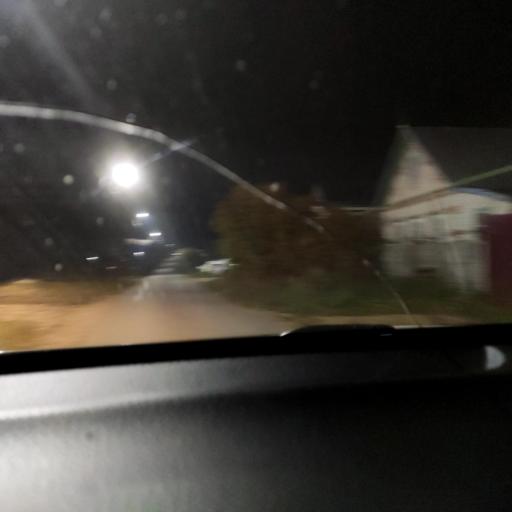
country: RU
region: Tatarstan
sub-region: Gorod Kazan'
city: Kazan
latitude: 55.8824
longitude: 49.0600
